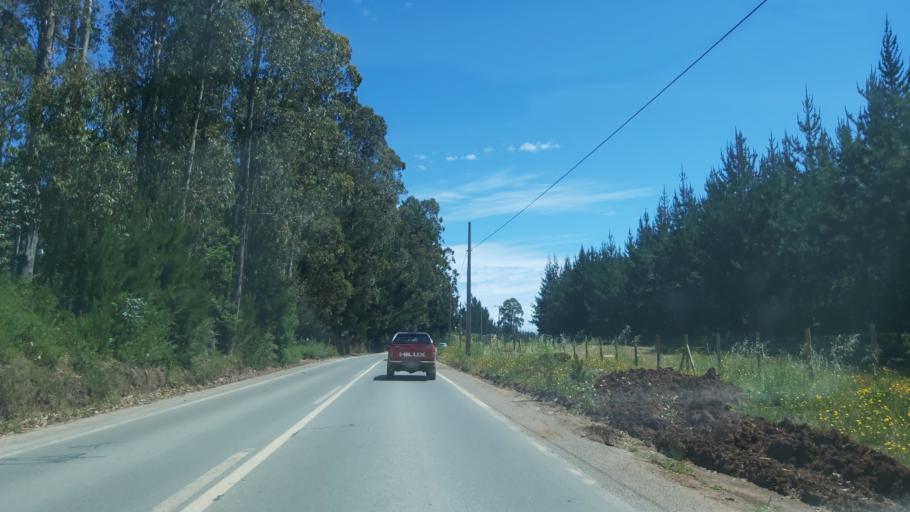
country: CL
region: Maule
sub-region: Provincia de Talca
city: Constitucion
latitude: -35.3964
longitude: -72.4307
